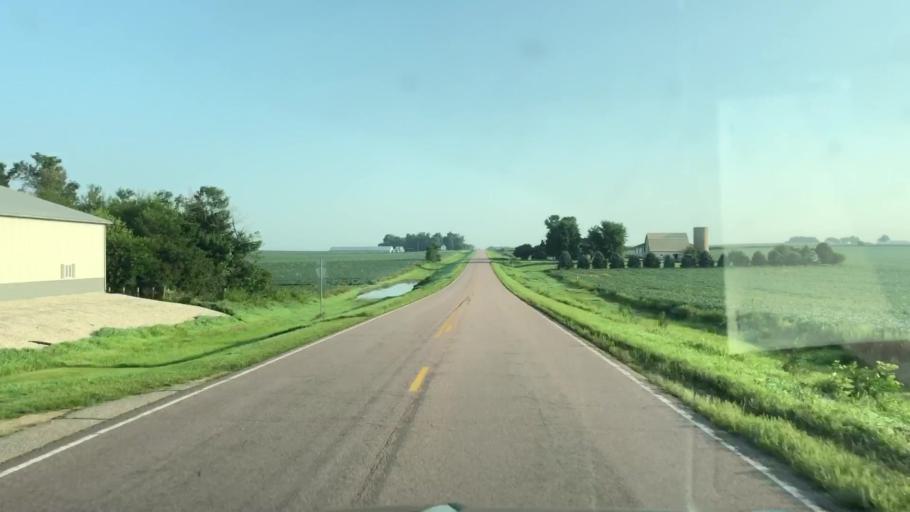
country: US
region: Iowa
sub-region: Lyon County
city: George
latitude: 43.2738
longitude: -95.9998
